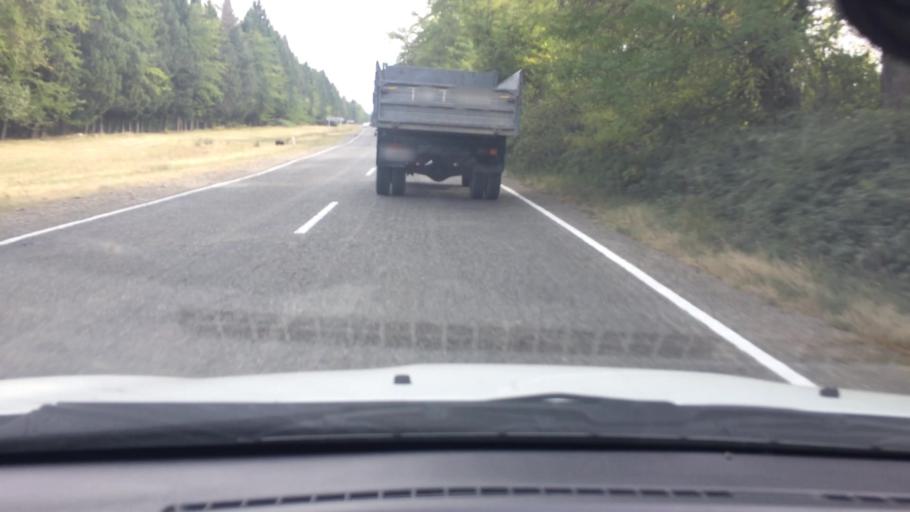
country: GE
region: Kvemo Kartli
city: Rust'avi
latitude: 41.4689
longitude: 44.9804
